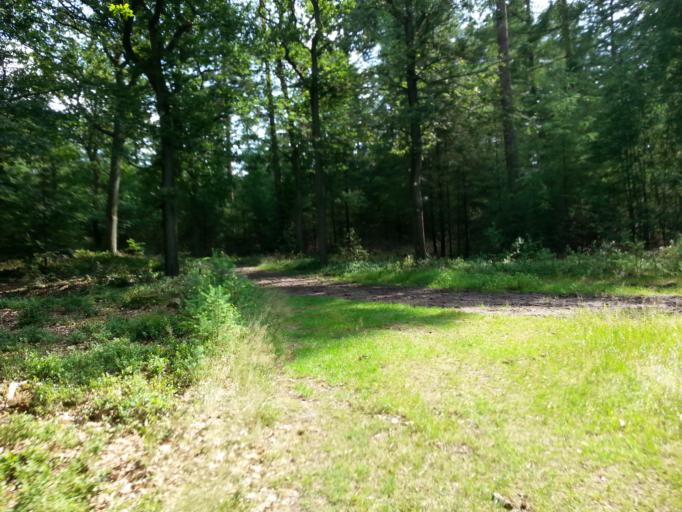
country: NL
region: Utrecht
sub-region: Gemeente Utrechtse Heuvelrug
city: Maarn
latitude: 52.0851
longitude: 5.3667
